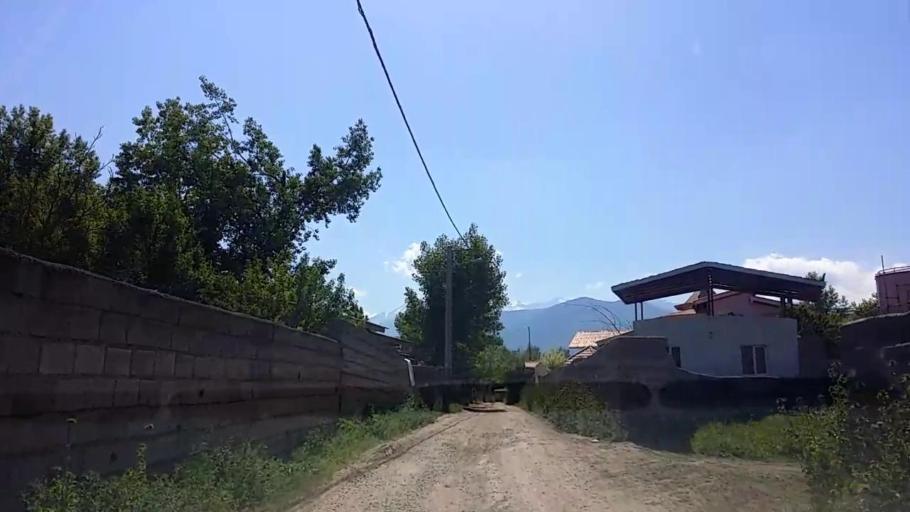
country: IR
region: Mazandaran
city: `Abbasabad
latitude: 36.5096
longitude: 51.2019
